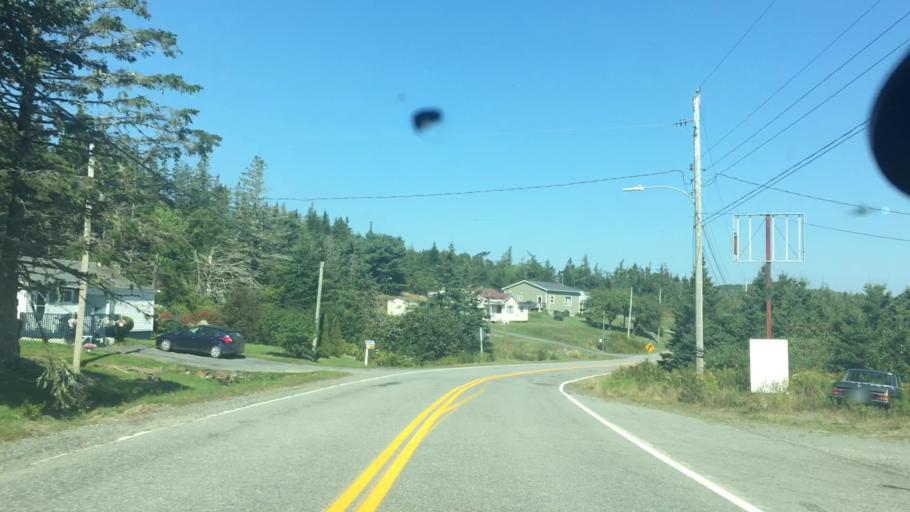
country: CA
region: Nova Scotia
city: New Glasgow
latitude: 44.9146
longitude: -62.3844
